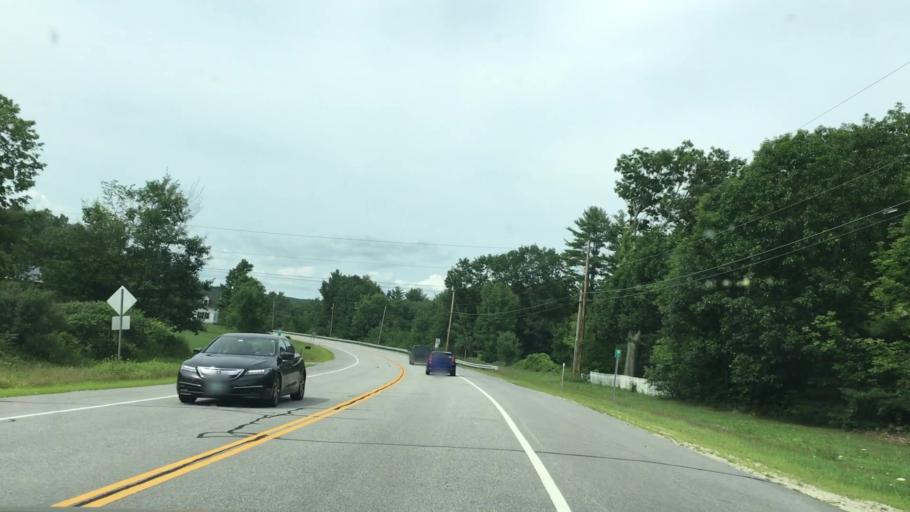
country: US
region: New Hampshire
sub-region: Hillsborough County
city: Hillsborough
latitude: 43.1031
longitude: -71.9155
